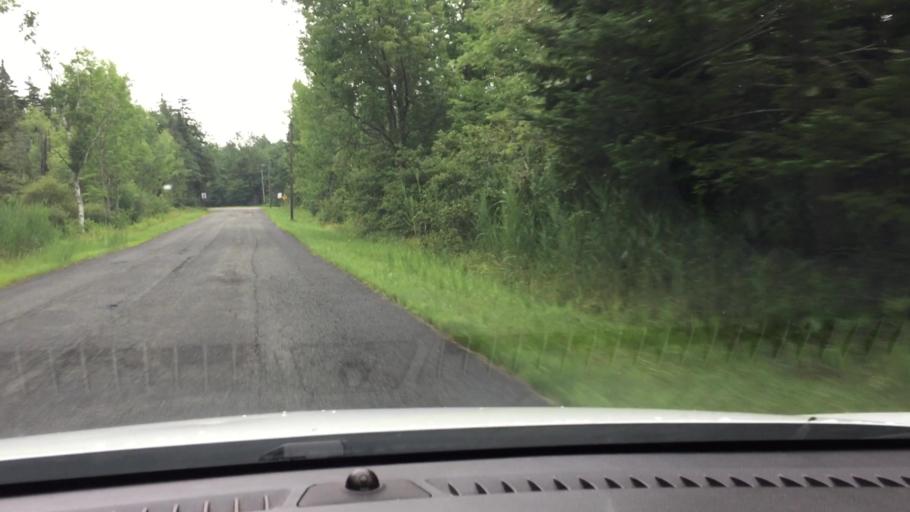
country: US
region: Massachusetts
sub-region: Berkshire County
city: Hinsdale
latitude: 42.4295
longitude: -73.0512
